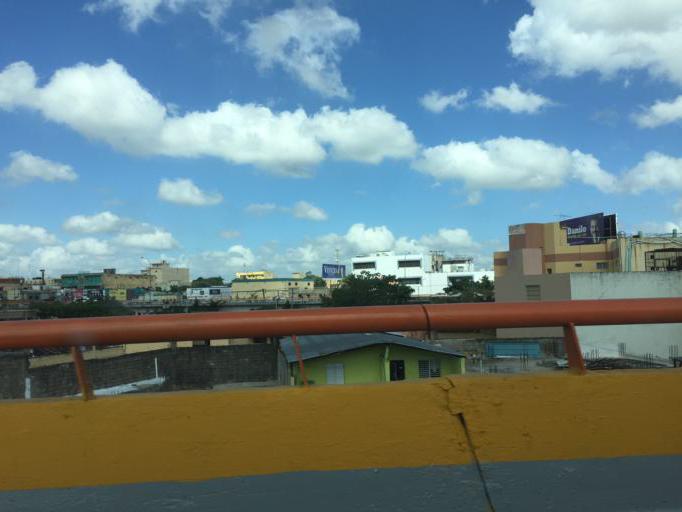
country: DO
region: Nacional
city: San Carlos
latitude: 18.4831
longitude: -69.8927
